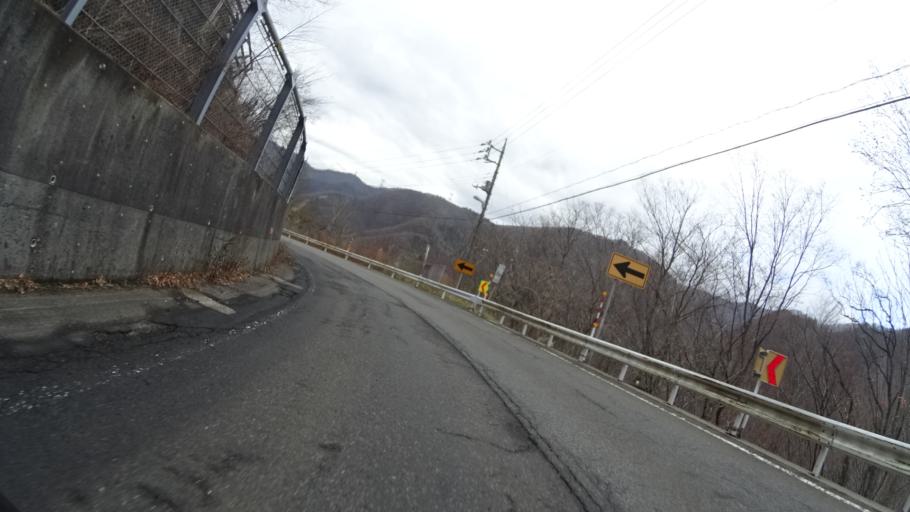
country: JP
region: Gunma
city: Nakanojomachi
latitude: 36.7405
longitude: 138.8342
